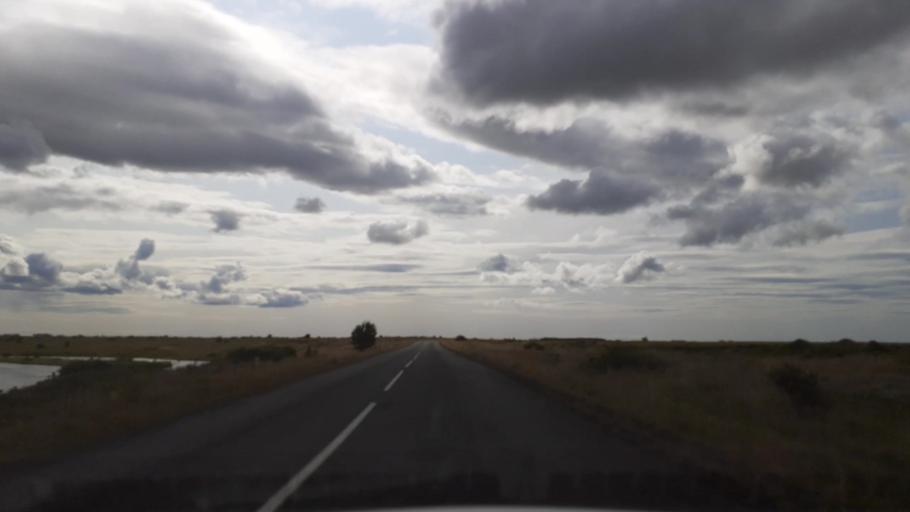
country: IS
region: South
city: Vestmannaeyjar
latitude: 63.8250
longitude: -20.4280
